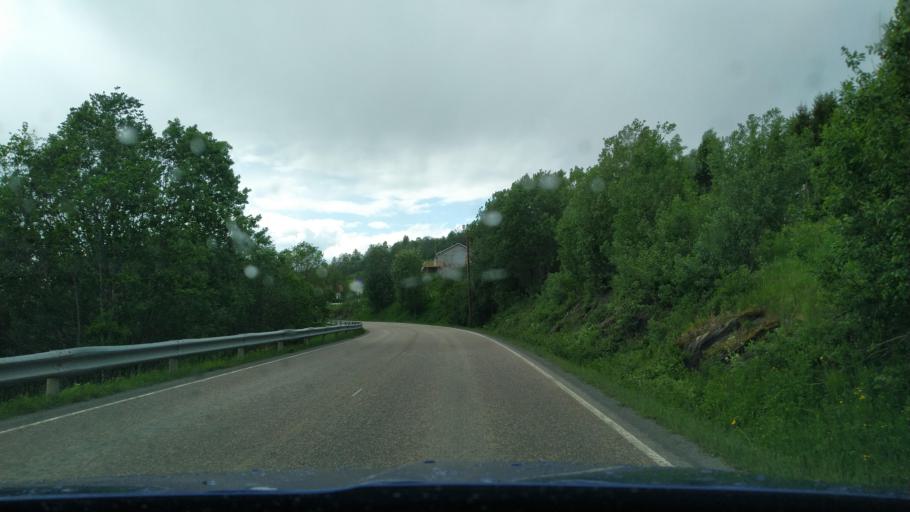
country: NO
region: Troms
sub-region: Sorreisa
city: Sorreisa
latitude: 69.1597
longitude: 18.1528
